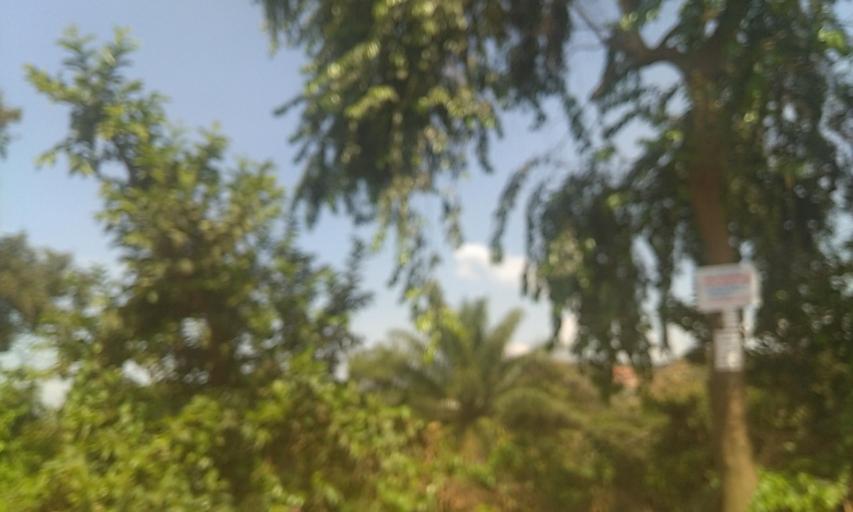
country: UG
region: Central Region
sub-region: Wakiso District
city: Kireka
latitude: 0.3745
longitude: 32.6009
